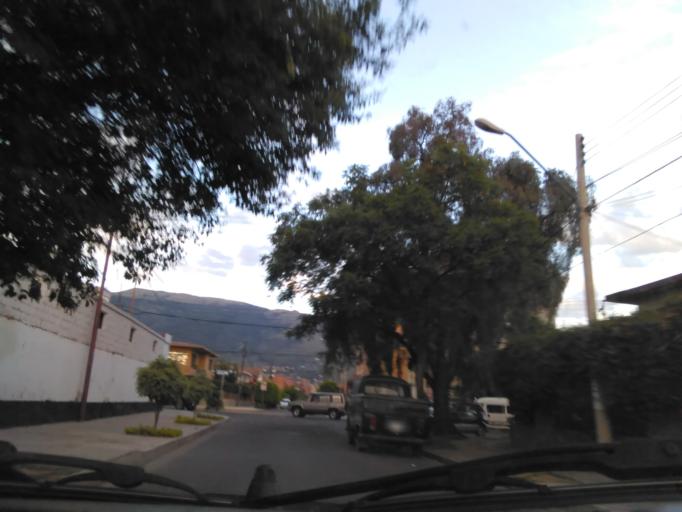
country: BO
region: Cochabamba
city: Cochabamba
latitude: -17.3860
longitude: -66.1674
